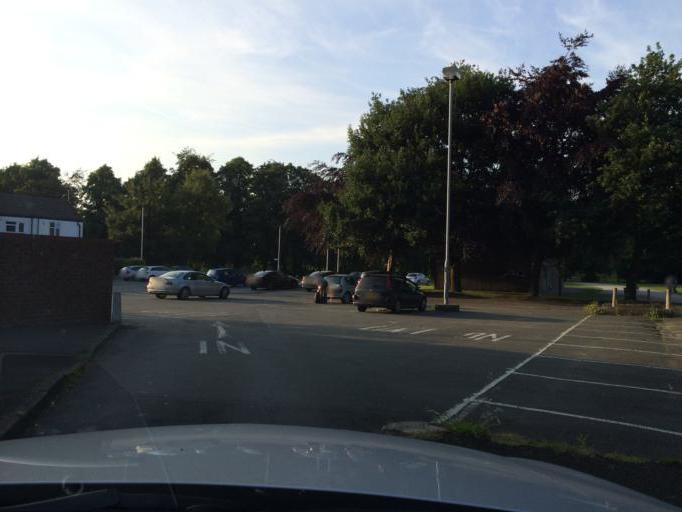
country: GB
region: England
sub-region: Borough of Stockport
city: Hazel Grove
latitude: 53.3754
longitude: -2.1126
